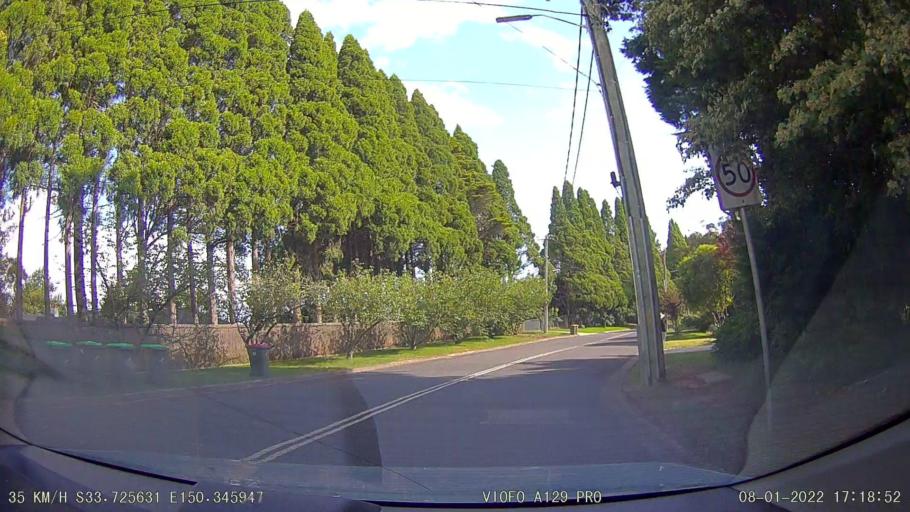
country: AU
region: New South Wales
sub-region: Blue Mountains Municipality
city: Leura
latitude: -33.7256
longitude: 150.3459
